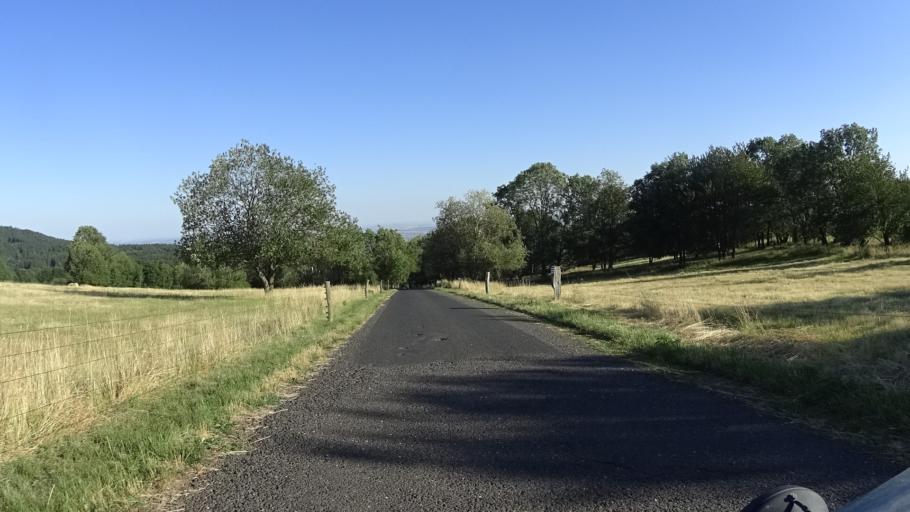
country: CZ
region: Ustecky
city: Zitenice
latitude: 50.5886
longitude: 14.1230
